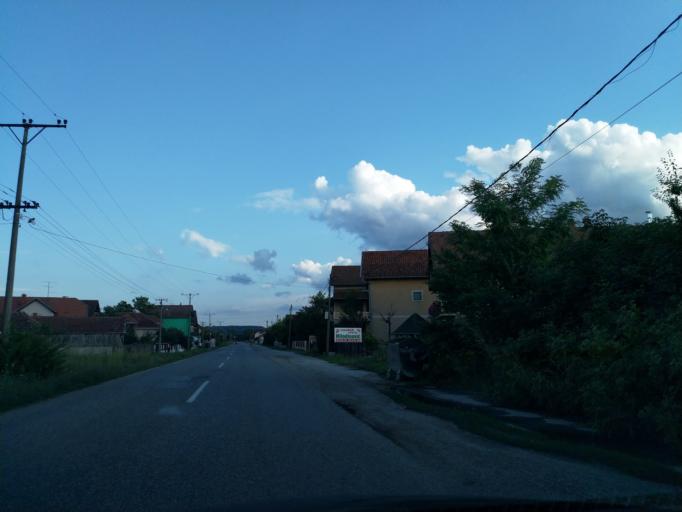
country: RS
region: Central Serbia
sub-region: Rasinski Okrug
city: Cicevac
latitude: 43.7617
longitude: 21.4311
